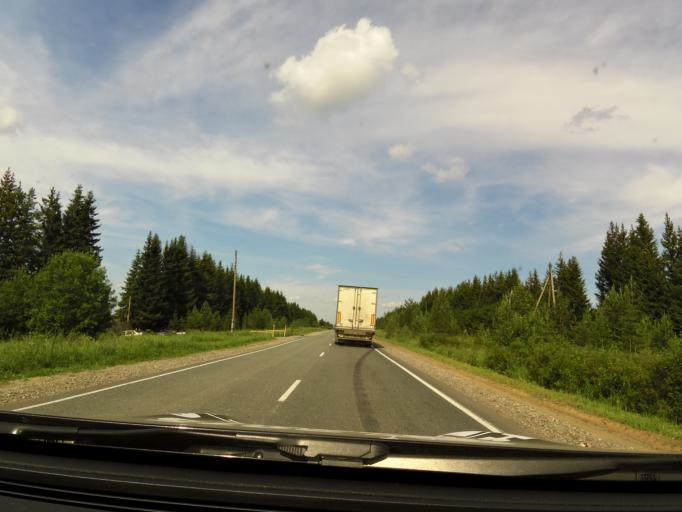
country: RU
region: Kirov
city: Slobodskoy
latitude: 58.7370
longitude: 50.2919
